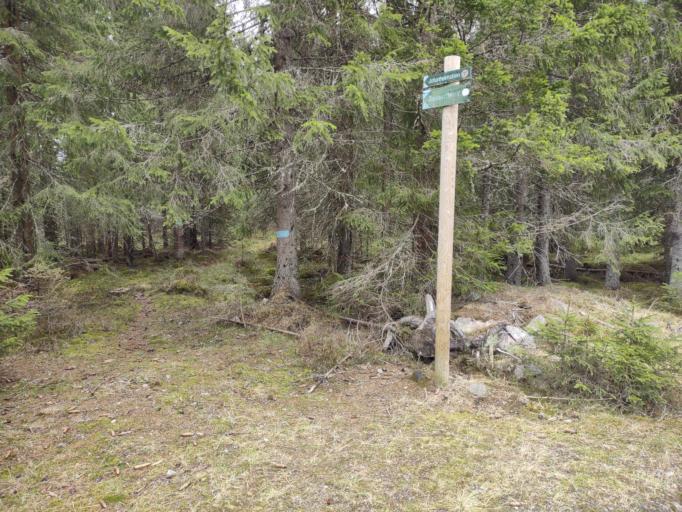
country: NO
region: Oppland
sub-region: Lunner
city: Roa
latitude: 60.3901
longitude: 10.7233
